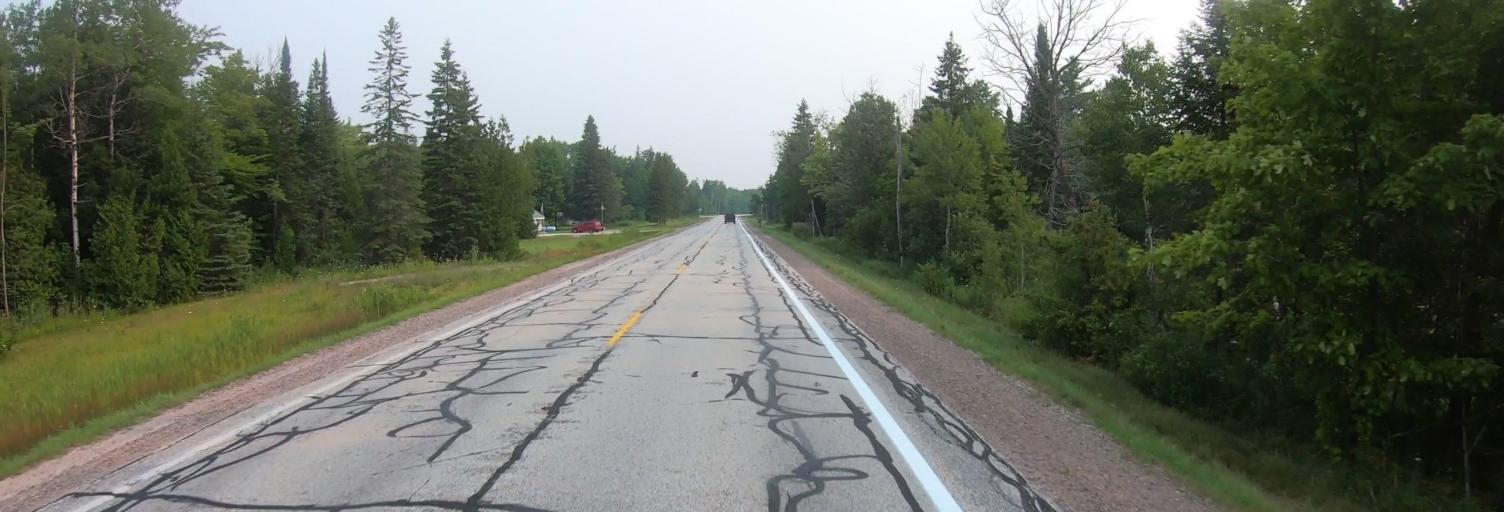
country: US
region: Michigan
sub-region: Luce County
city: Newberry
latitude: 46.5052
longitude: -85.0930
